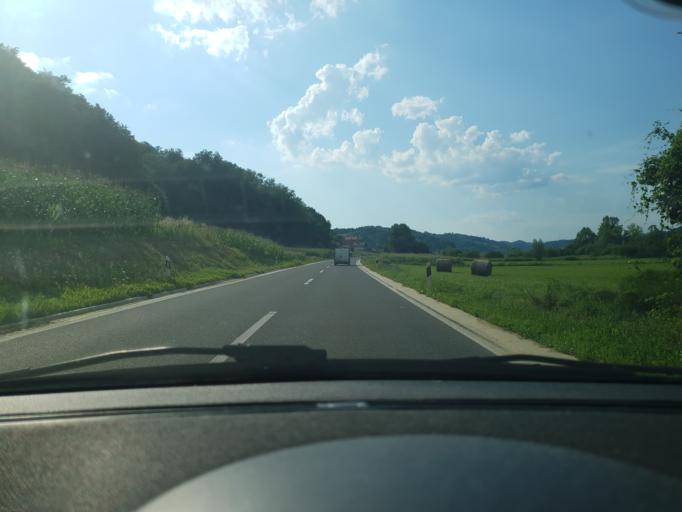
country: HR
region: Zagrebacka
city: Jakovlje
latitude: 46.0370
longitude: 15.8219
